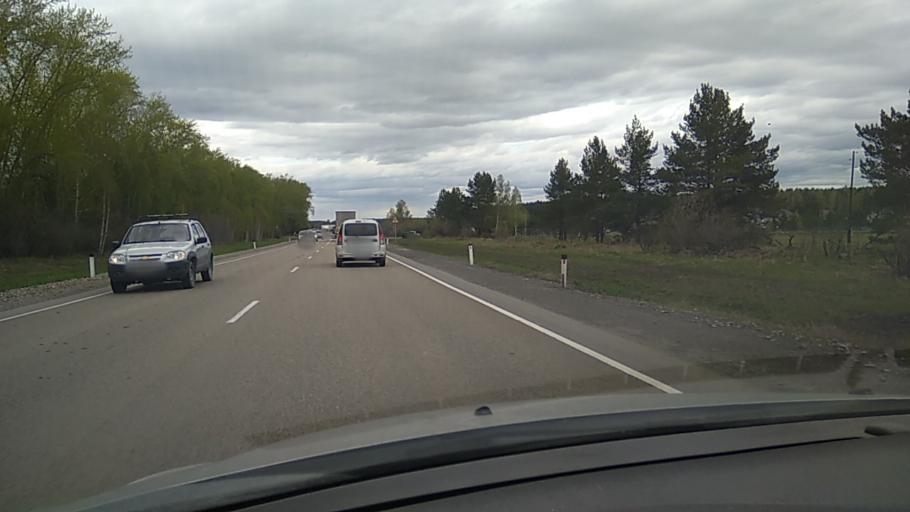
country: RU
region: Sverdlovsk
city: Dvurechensk
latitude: 56.6714
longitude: 61.1462
